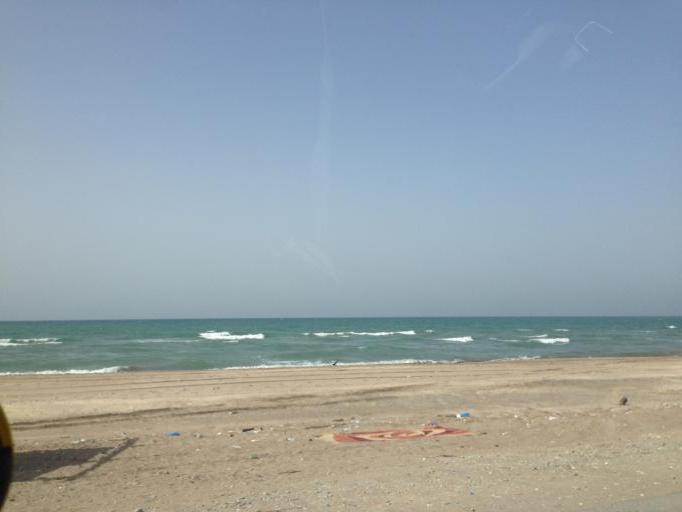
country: OM
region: Al Batinah
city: Barka'
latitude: 23.7112
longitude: 57.8838
